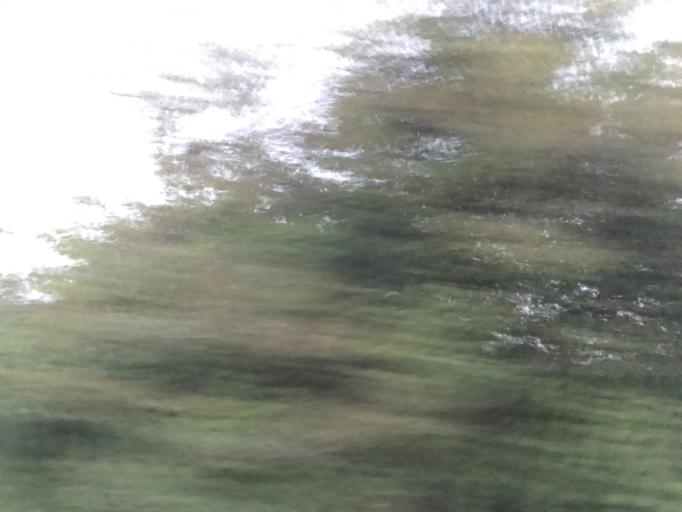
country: TR
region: Hatay
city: Uzunbag
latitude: 36.1175
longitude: 36.0476
